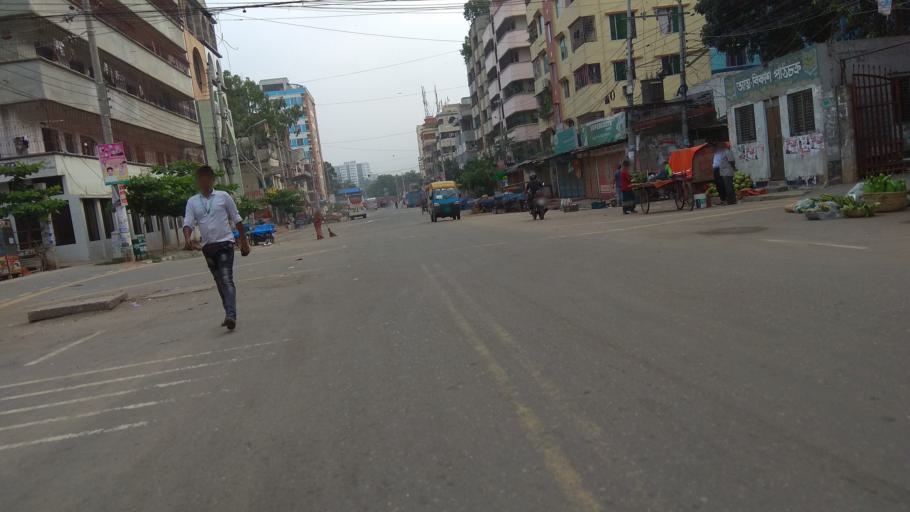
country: BD
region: Dhaka
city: Tungi
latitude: 23.8268
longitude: 90.3661
